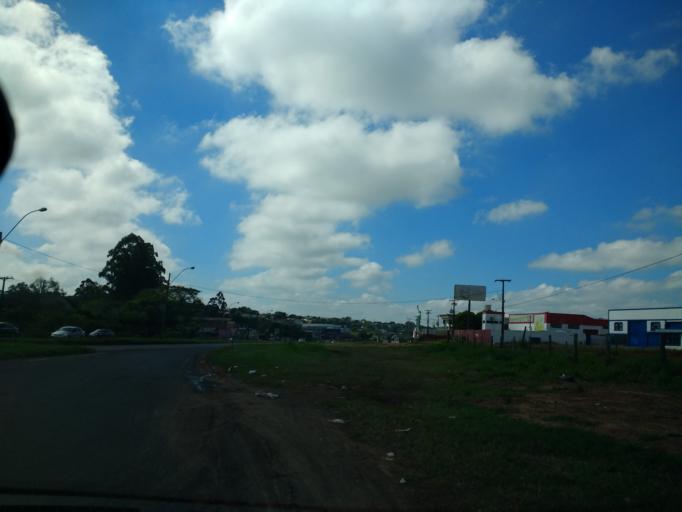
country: BR
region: Parana
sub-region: Umuarama
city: Umuarama
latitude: -23.7806
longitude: -53.3046
